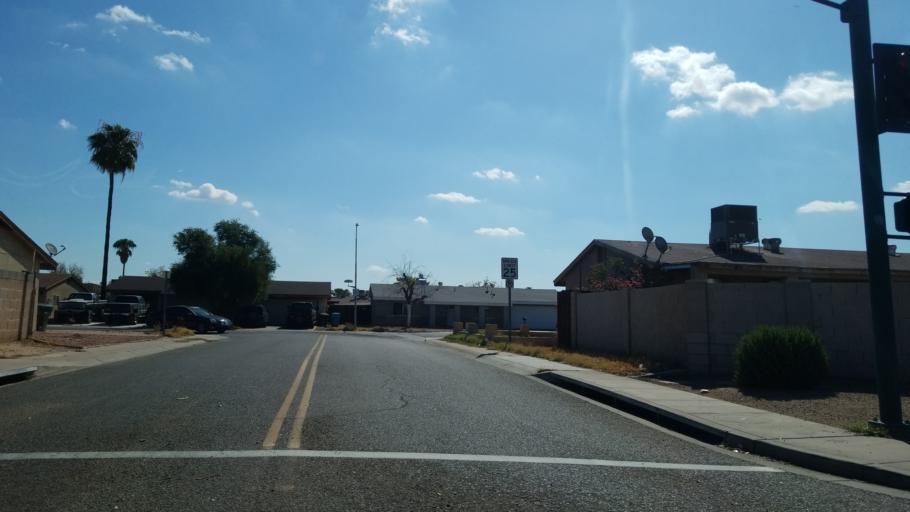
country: US
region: Arizona
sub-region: Maricopa County
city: Tolleson
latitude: 33.4980
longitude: -112.2377
